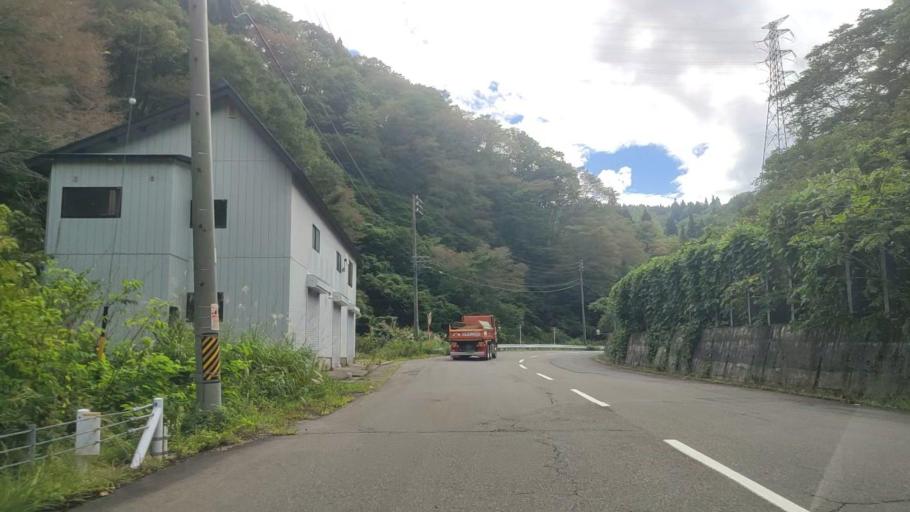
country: JP
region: Nagano
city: Iiyama
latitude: 36.8918
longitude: 138.3230
